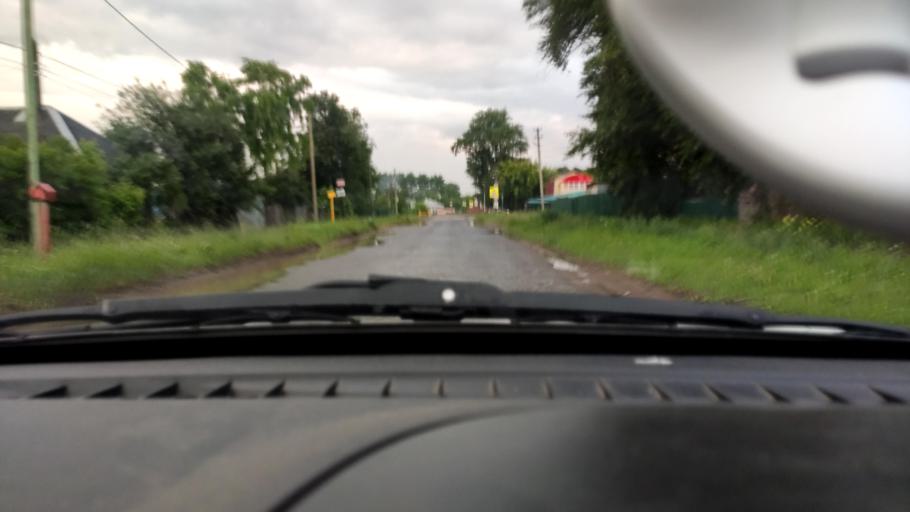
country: RU
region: Perm
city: Kultayevo
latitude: 57.9330
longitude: 56.0192
